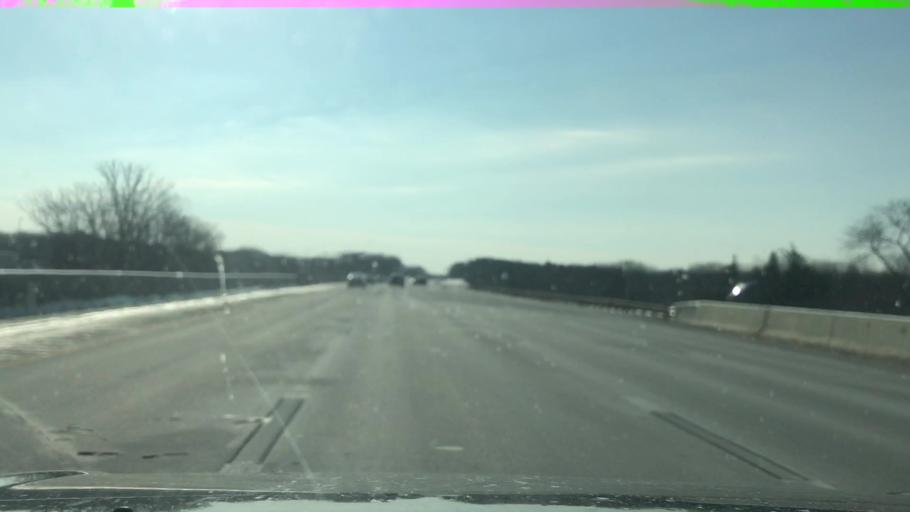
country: US
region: New Jersey
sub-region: Monmouth County
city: Ramtown
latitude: 40.1631
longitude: -74.1025
